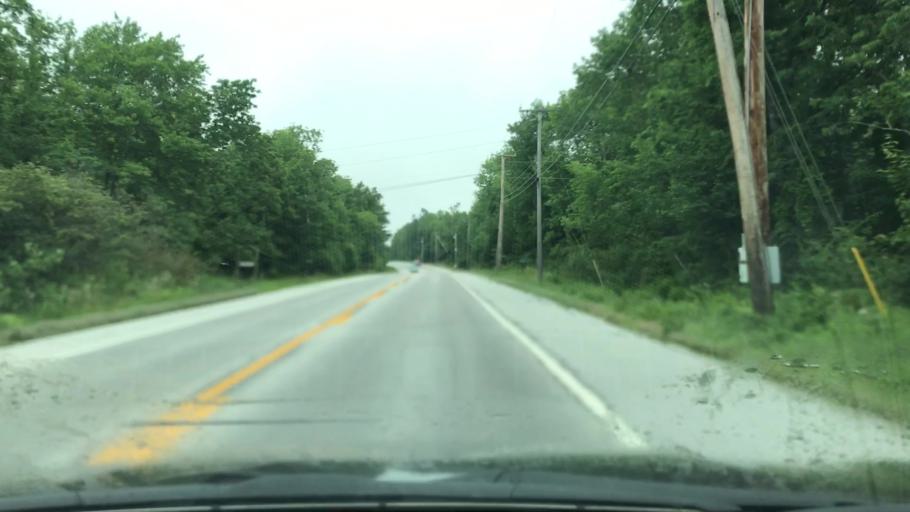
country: US
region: Maine
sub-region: Waldo County
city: Northport
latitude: 44.3228
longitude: -68.9629
